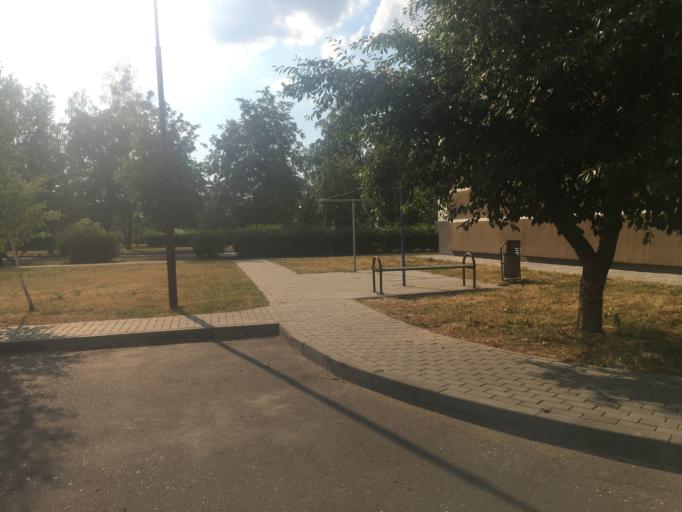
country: BY
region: Grodnenskaya
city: Hrodna
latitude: 53.6660
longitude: 23.8017
